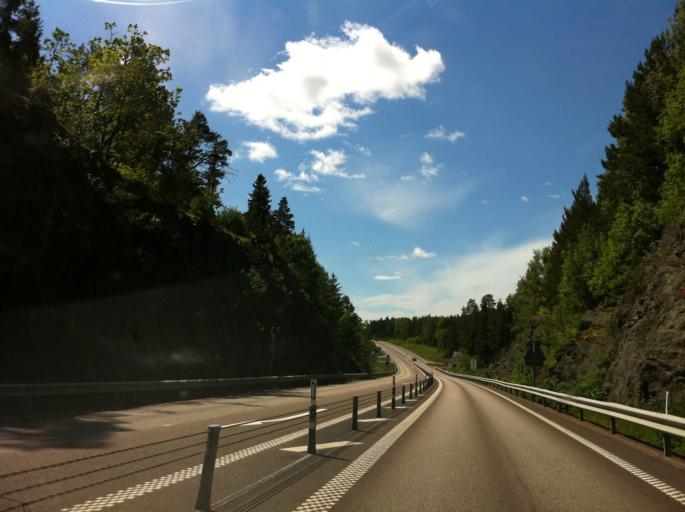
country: SE
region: Vaestra Goetaland
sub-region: Melleruds Kommun
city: Mellerud
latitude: 58.7767
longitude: 12.5006
